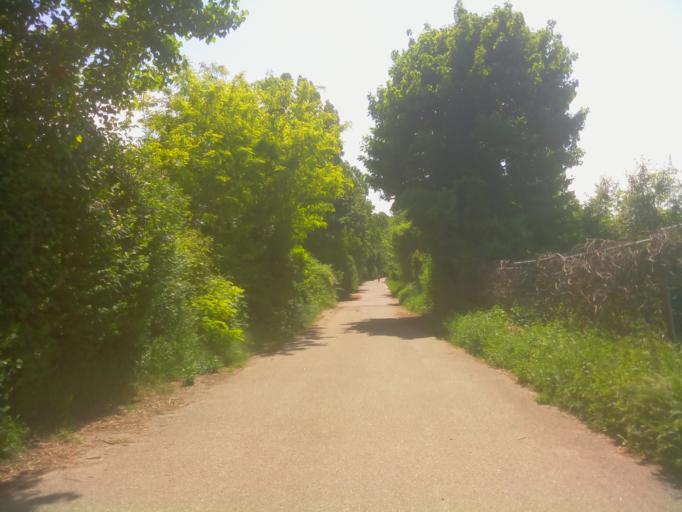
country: DE
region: Rheinland-Pfalz
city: Neuhofen
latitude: 49.4466
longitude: 8.4310
